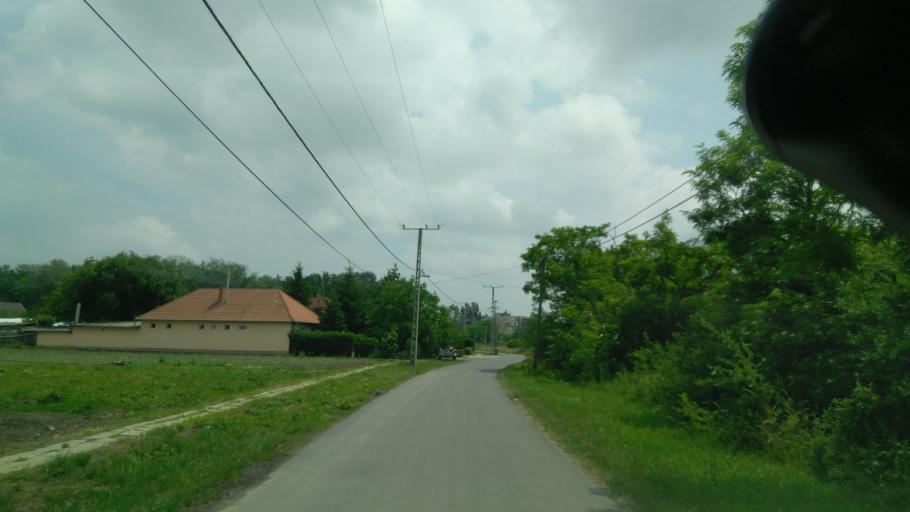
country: HU
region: Bekes
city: Gyula
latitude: 46.6579
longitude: 21.2552
